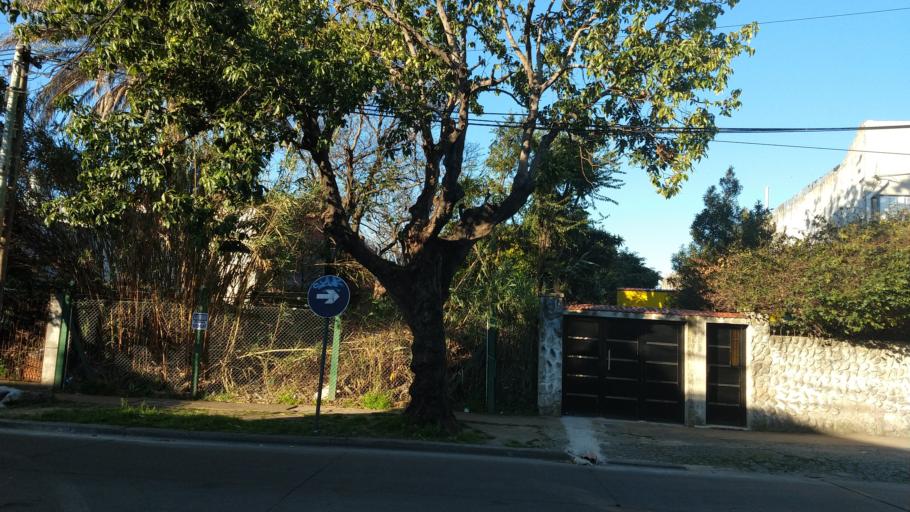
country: AR
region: Buenos Aires
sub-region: Partido de Vicente Lopez
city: Olivos
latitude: -34.5239
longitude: -58.5282
